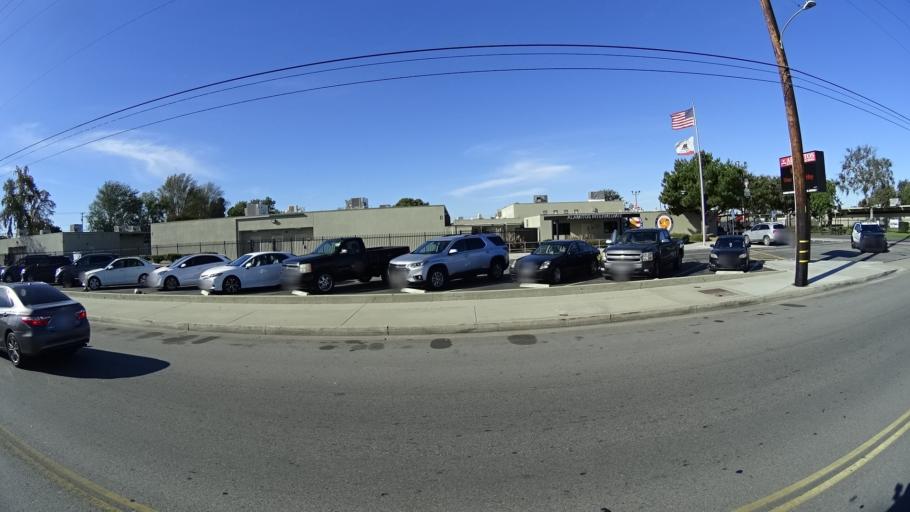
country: US
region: California
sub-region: Orange County
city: Stanton
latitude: 33.7823
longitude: -117.9843
